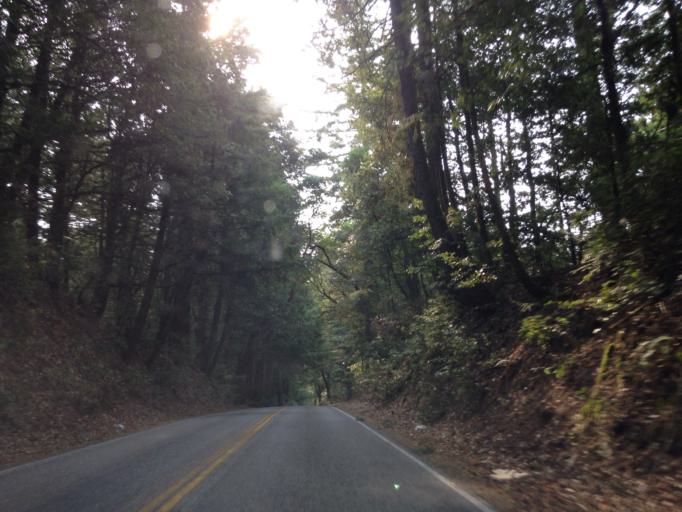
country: US
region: California
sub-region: San Mateo County
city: Woodside
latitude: 37.4161
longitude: -122.3154
